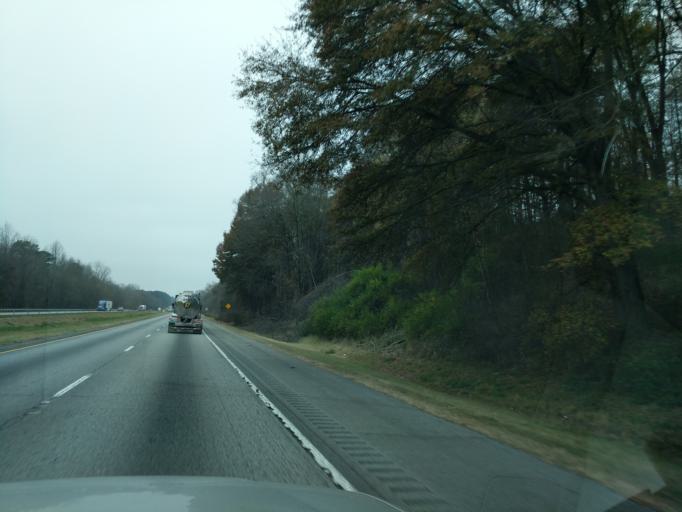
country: US
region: Georgia
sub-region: Franklin County
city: Carnesville
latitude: 34.3729
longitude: -83.2650
